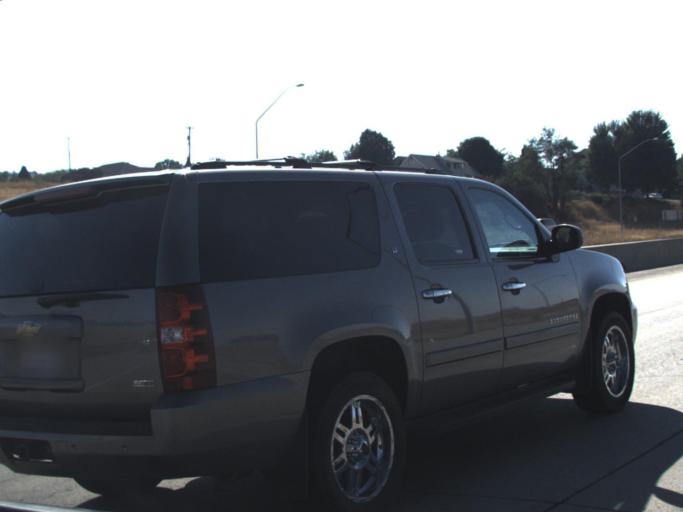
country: US
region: Washington
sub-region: Spokane County
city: Spokane Valley
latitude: 47.6741
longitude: -117.2420
